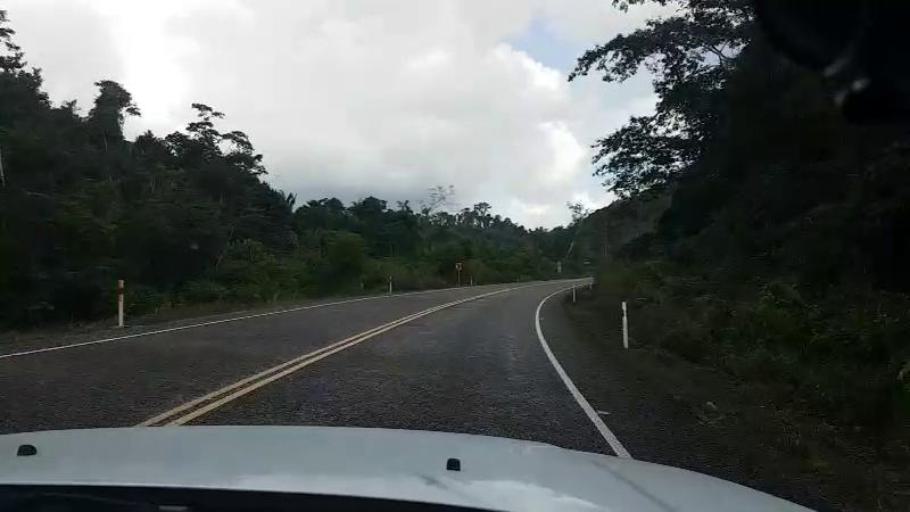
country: BZ
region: Cayo
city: Belmopan
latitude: 17.1583
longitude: -88.6881
